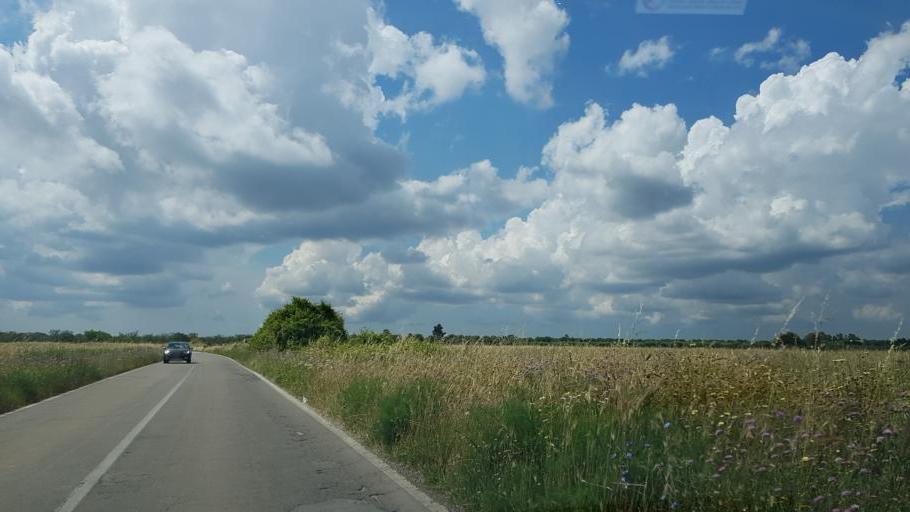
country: IT
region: Apulia
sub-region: Provincia di Brindisi
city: Mesagne
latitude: 40.5235
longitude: 17.8212
